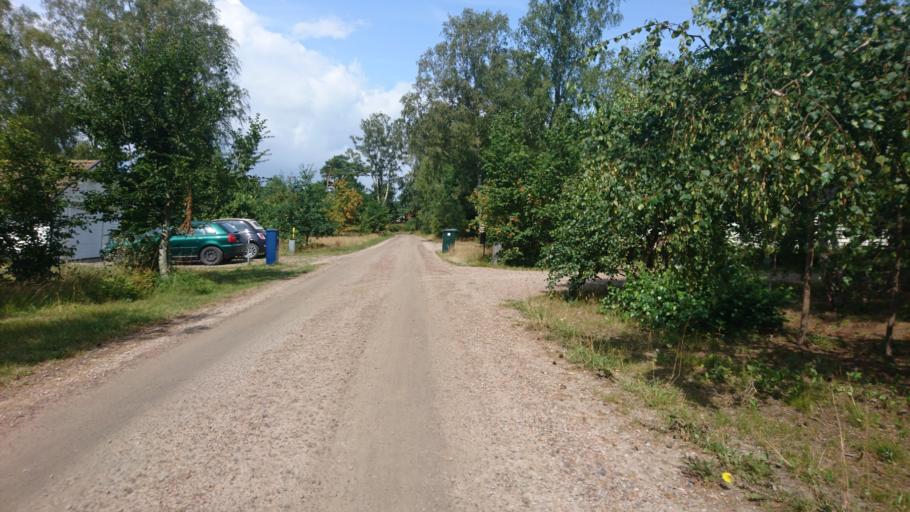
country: SE
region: Skane
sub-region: Vellinge Kommun
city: Ljunghusen
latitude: 55.3918
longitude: 12.9117
